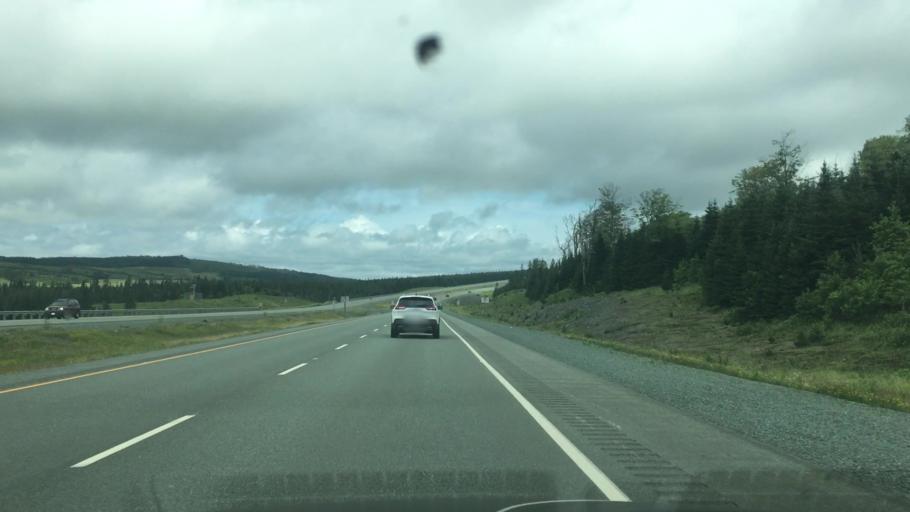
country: CA
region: Nova Scotia
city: Oxford
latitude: 45.5467
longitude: -63.7115
